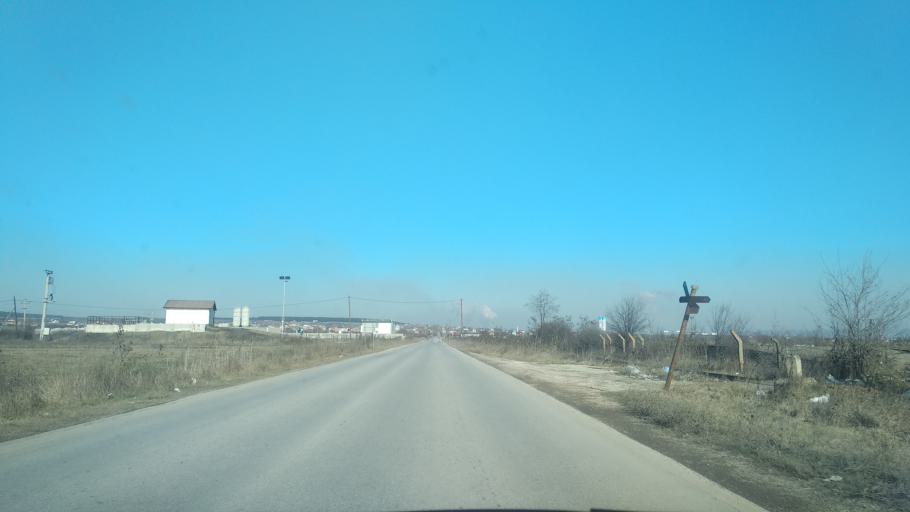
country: XK
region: Pristina
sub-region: Komuna e Gracanices
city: Glanica
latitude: 42.5827
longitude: 21.0157
